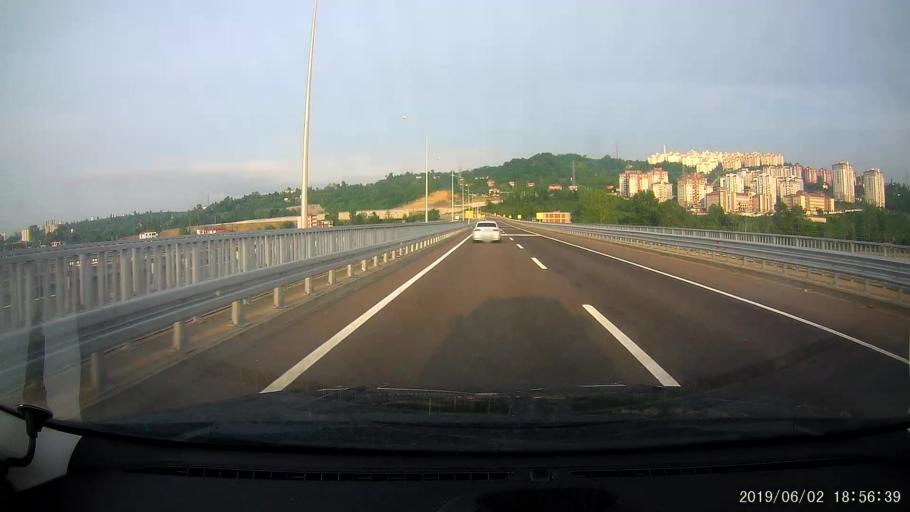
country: TR
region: Ordu
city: Ordu
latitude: 40.9546
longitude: 37.8962
